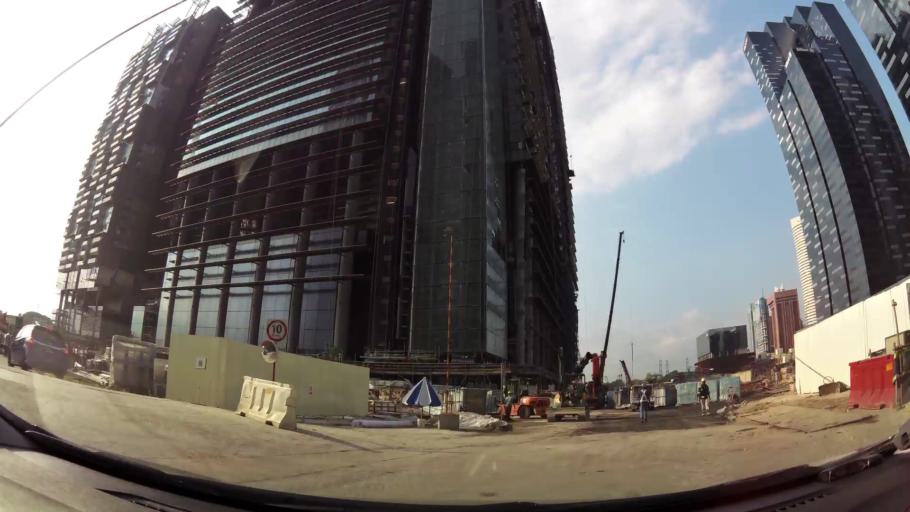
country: SG
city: Singapore
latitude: 1.2788
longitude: 103.8529
